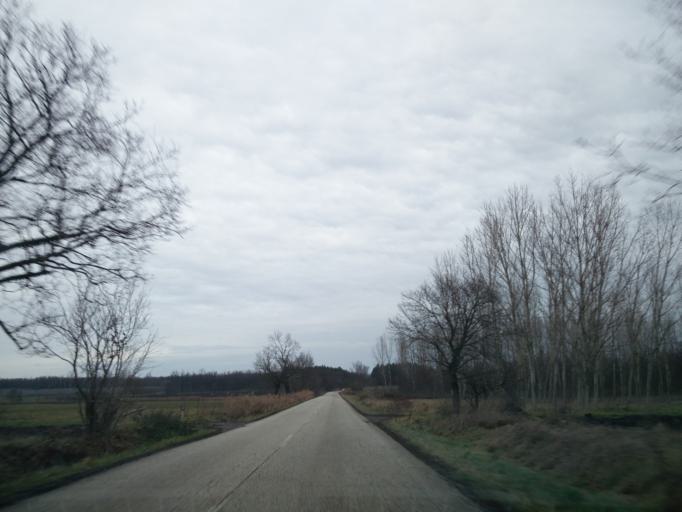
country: HU
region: Pest
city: Suelysap
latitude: 47.4656
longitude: 19.5565
